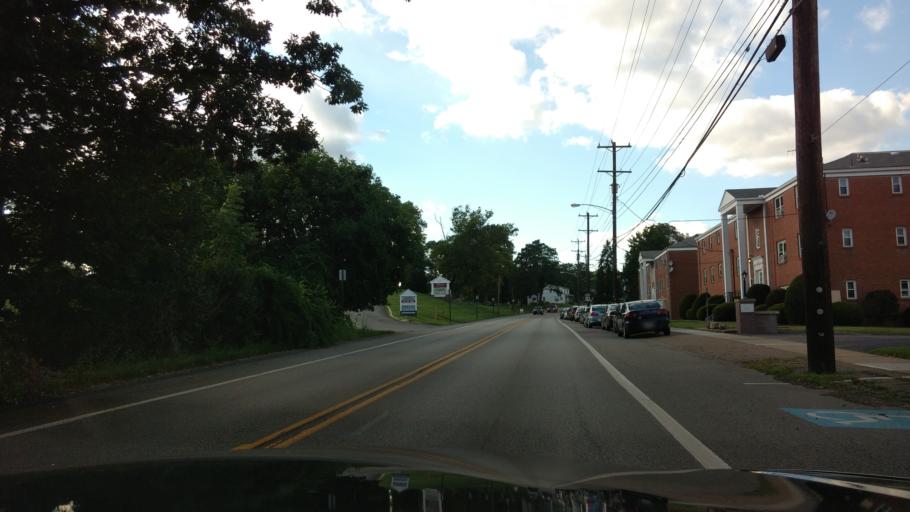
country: US
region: Pennsylvania
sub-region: Allegheny County
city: West View
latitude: 40.5303
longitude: -80.0352
